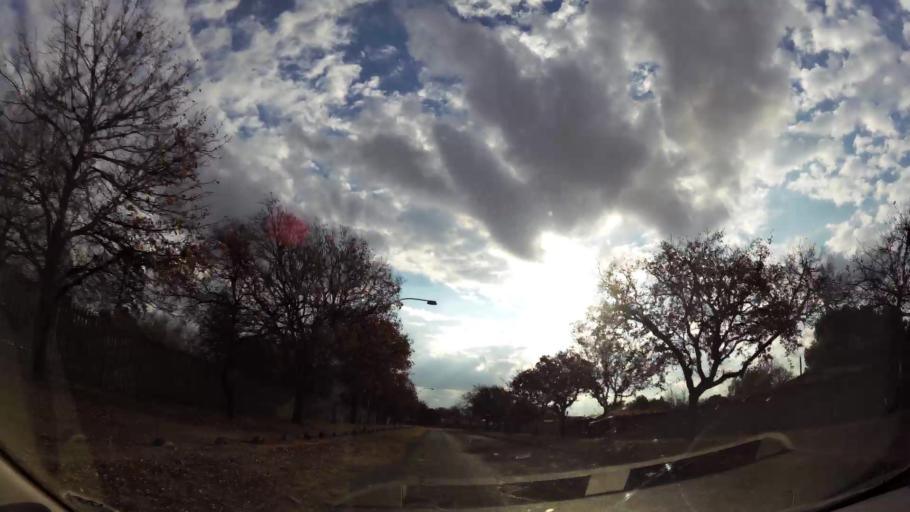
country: ZA
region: Orange Free State
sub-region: Fezile Dabi District Municipality
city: Sasolburg
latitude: -26.8265
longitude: 27.8182
